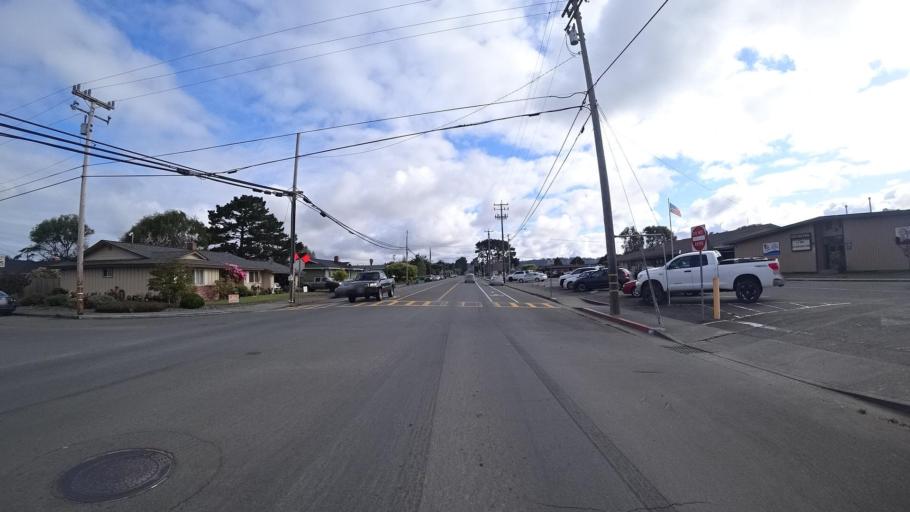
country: US
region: California
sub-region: Humboldt County
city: Arcata
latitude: 40.8948
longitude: -124.0938
